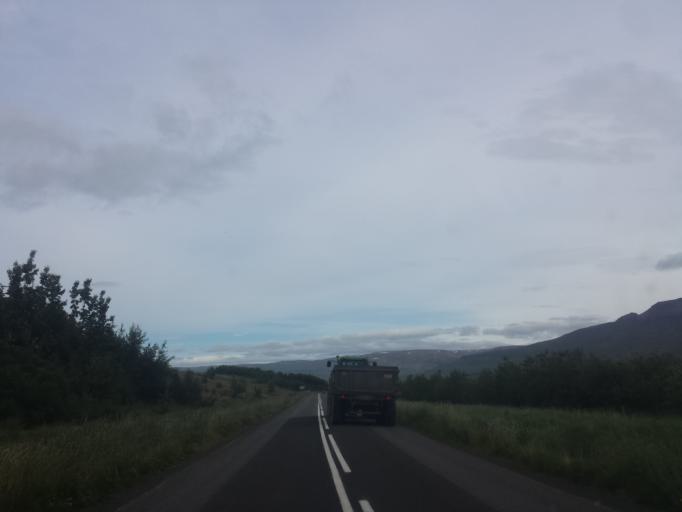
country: IS
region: Northeast
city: Akureyri
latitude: 65.5266
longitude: -18.1487
